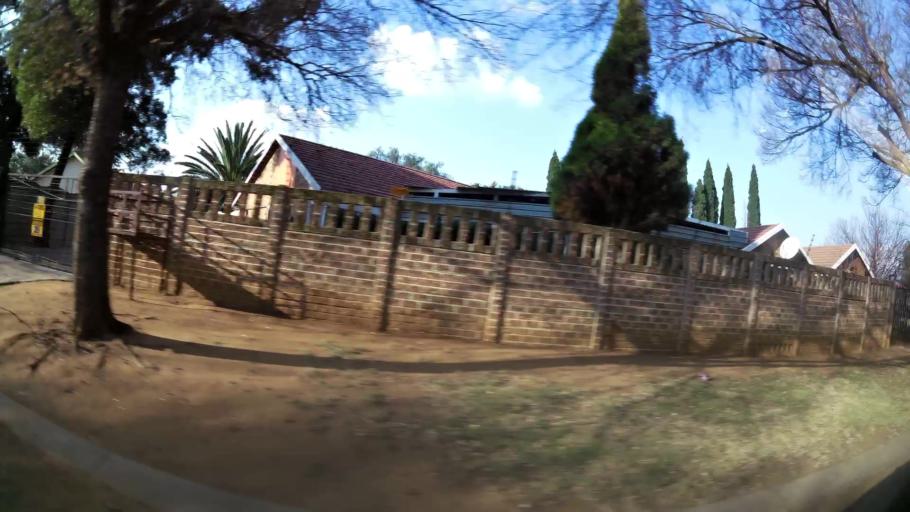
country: ZA
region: Gauteng
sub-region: Ekurhuleni Metropolitan Municipality
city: Benoni
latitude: -26.1291
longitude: 28.3755
